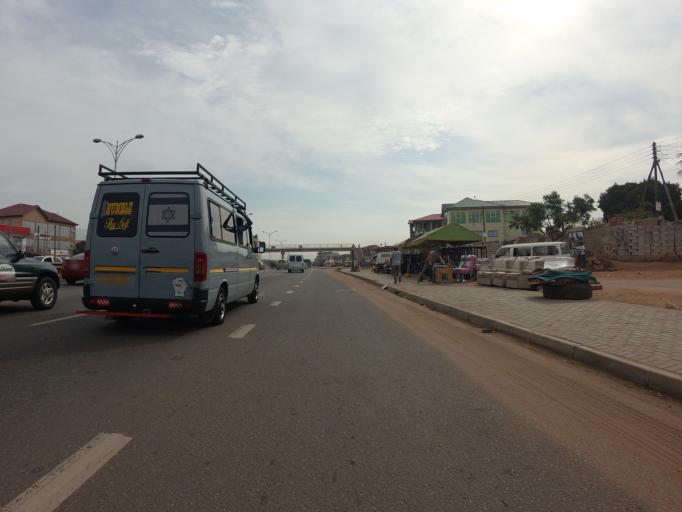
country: GH
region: Greater Accra
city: Dome
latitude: 5.6042
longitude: -0.2546
